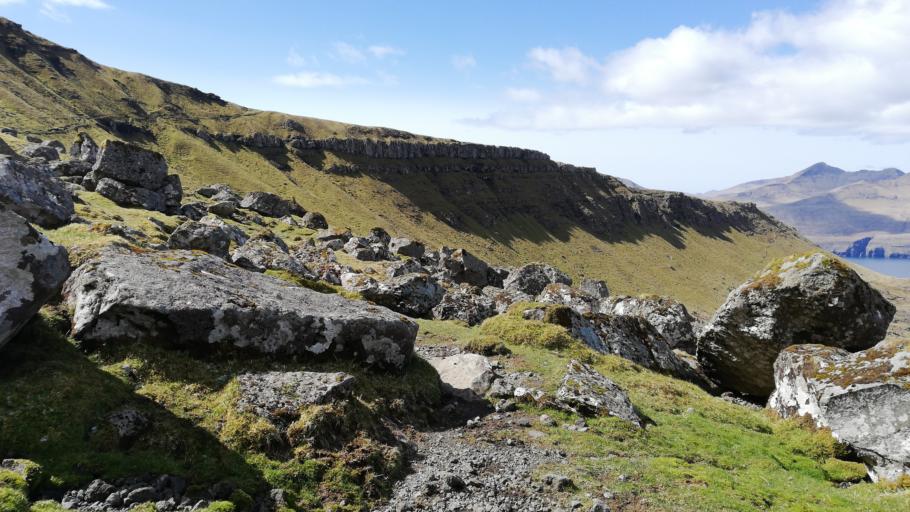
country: FO
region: Streymoy
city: Kollafjordhur
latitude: 62.0704
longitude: -6.9750
